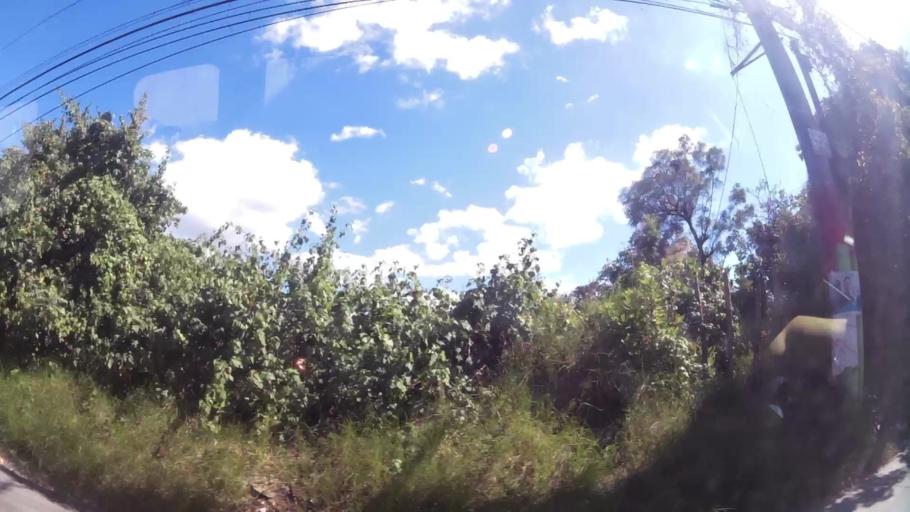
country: GT
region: Guatemala
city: Petapa
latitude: 14.4987
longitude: -90.5627
